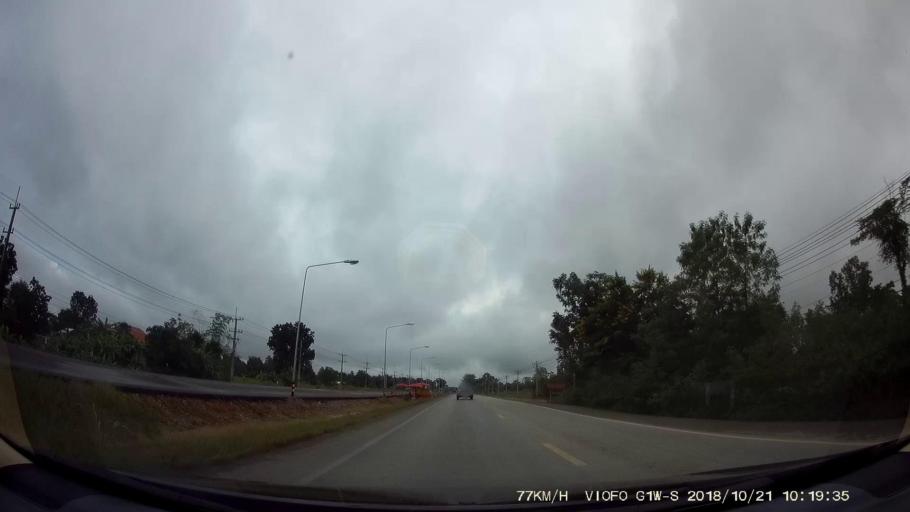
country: TH
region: Chaiyaphum
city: Phu Khiao
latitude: 16.3133
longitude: 102.1996
